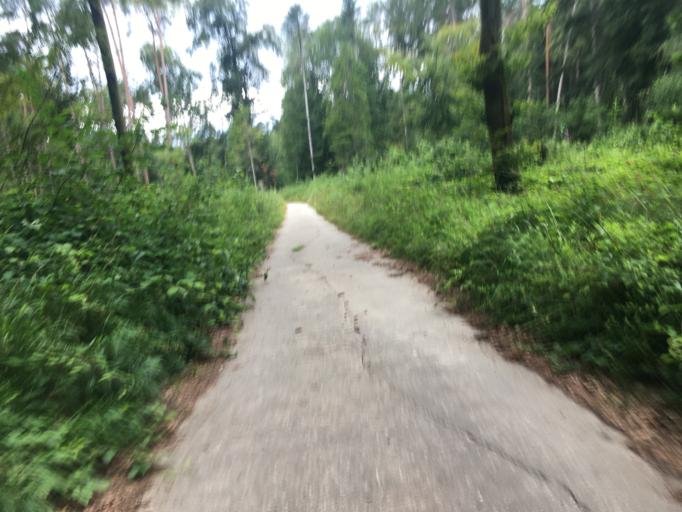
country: CH
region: Fribourg
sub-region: Broye District
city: Estavayer-le-Lac
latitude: 46.8707
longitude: 6.8979
